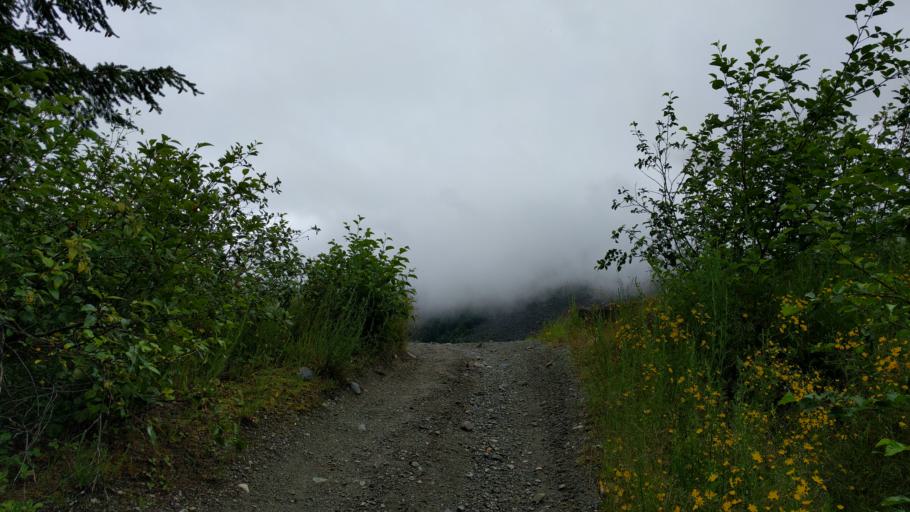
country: CA
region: British Columbia
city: Hope
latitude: 49.2979
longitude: -121.2631
